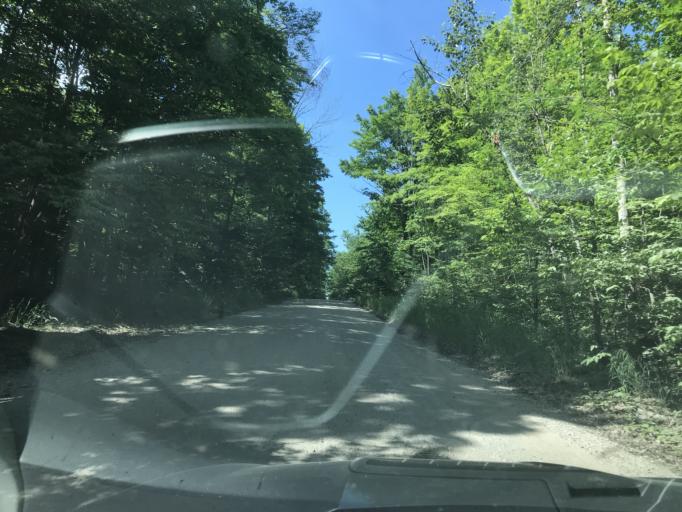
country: US
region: Michigan
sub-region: Cheboygan County
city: Cheboygan
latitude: 45.6064
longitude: -84.6714
